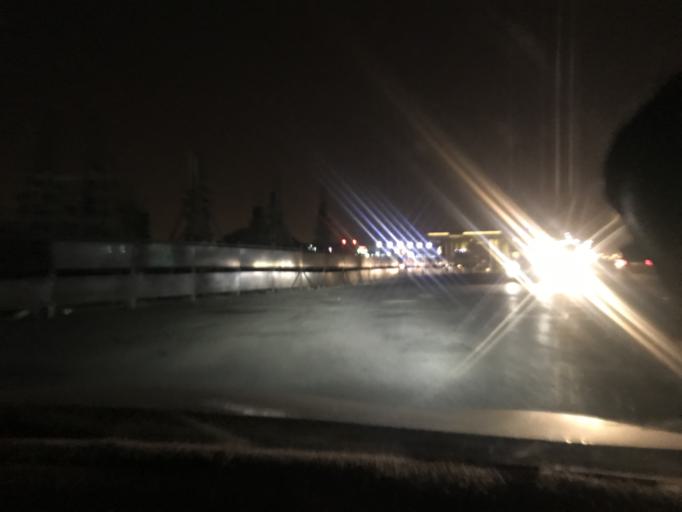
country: SA
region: Ar Riyad
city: Riyadh
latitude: 24.8517
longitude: 46.6020
